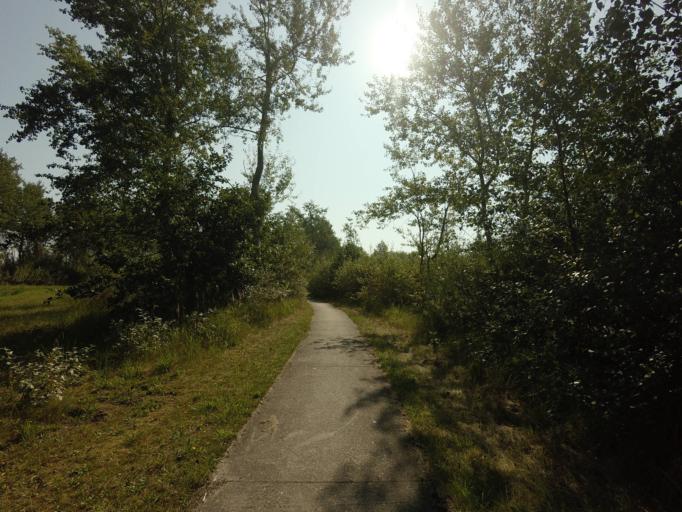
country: NL
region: Groningen
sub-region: Gemeente De Marne
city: Ulrum
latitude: 53.3932
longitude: 6.2540
